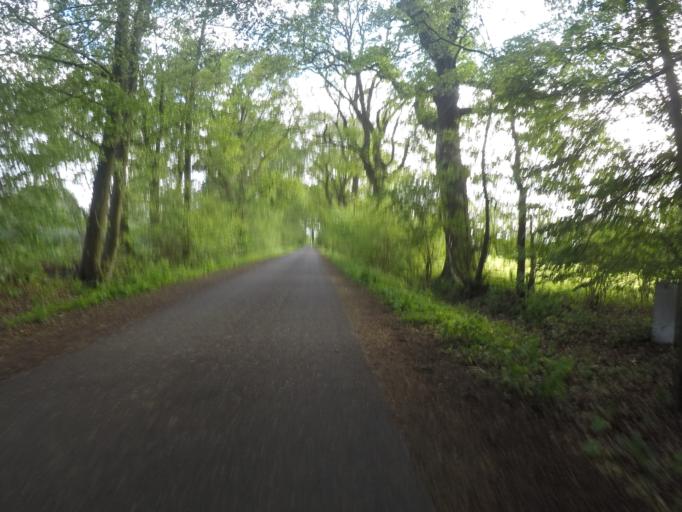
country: DE
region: Schleswig-Holstein
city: Bonningstedt
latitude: 53.6706
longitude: 9.9294
